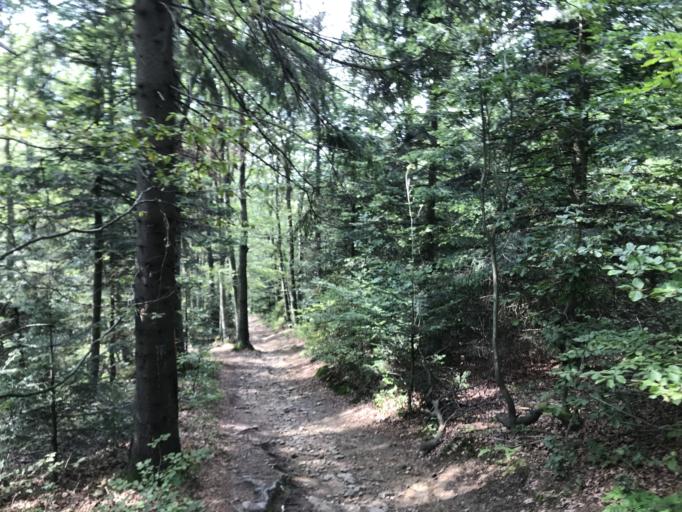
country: PL
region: Lesser Poland Voivodeship
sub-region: Powiat limanowski
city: Skrzydlna
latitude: 49.7152
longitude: 20.1771
